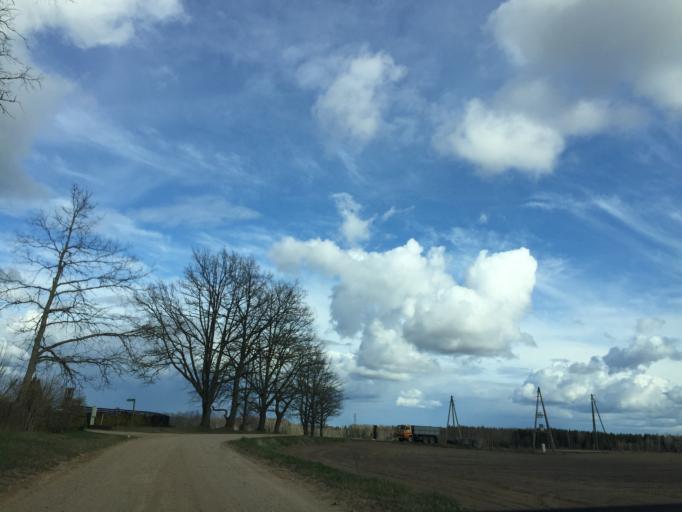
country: LV
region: Burtnieki
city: Matisi
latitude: 57.6123
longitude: 25.0214
